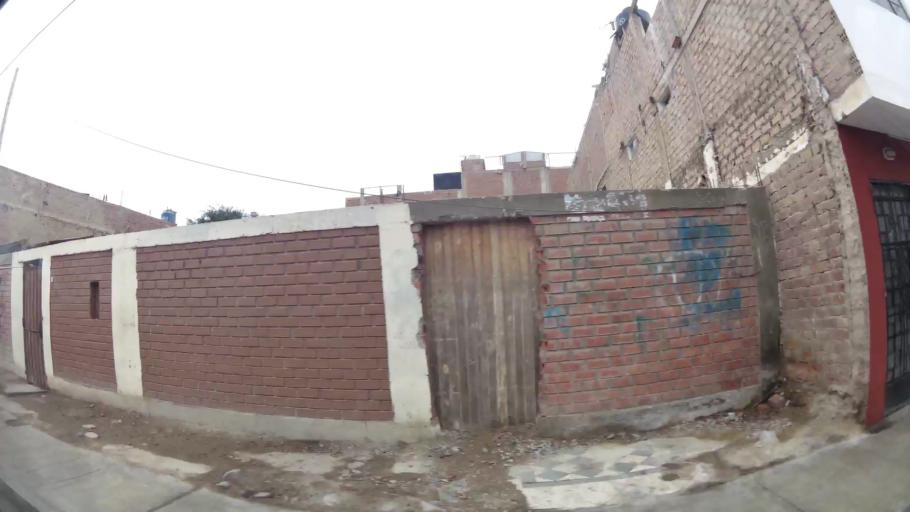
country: PE
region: Ica
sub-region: Provincia de Pisco
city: Pisco
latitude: -13.7116
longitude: -76.2003
